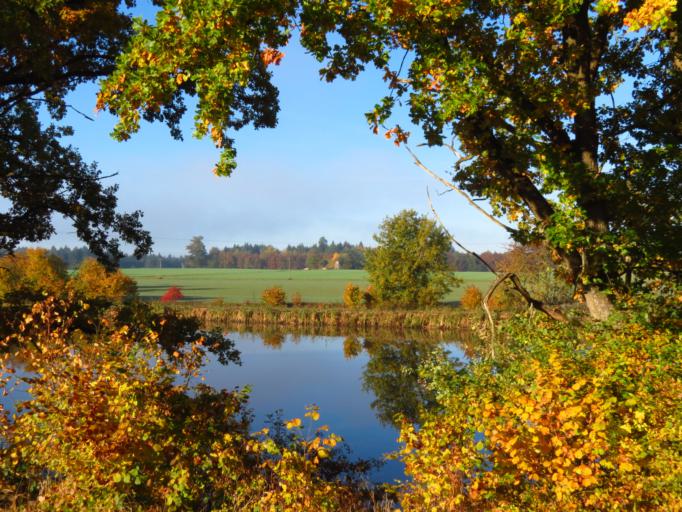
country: DE
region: Bavaria
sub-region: Regierungsbezirk Mittelfranken
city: Wilburgstetten
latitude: 49.0575
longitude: 10.3728
